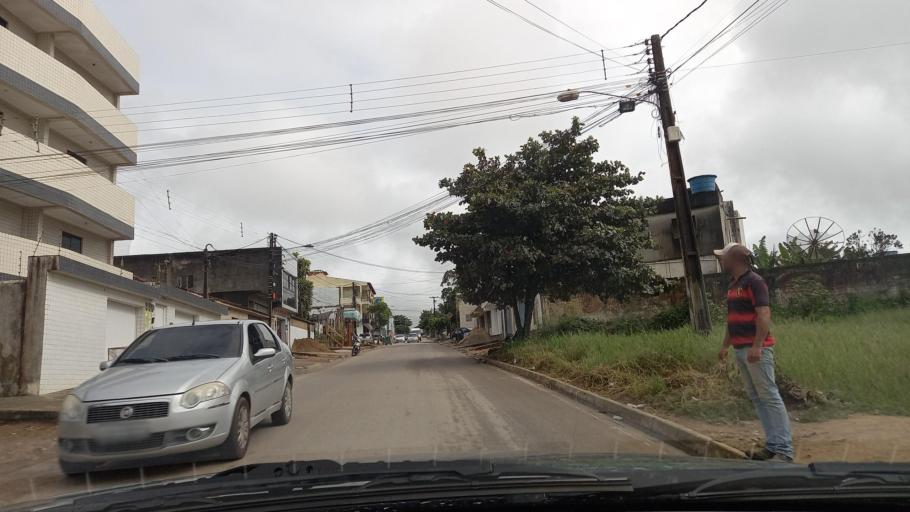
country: BR
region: Pernambuco
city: Garanhuns
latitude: -8.9071
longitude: -36.4883
